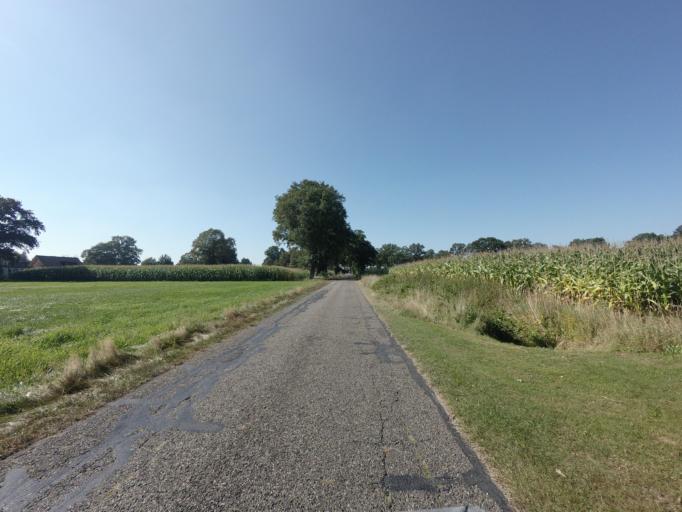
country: NL
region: Overijssel
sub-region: Gemeente Hardenberg
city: Hardenberg
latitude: 52.5281
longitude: 6.5962
